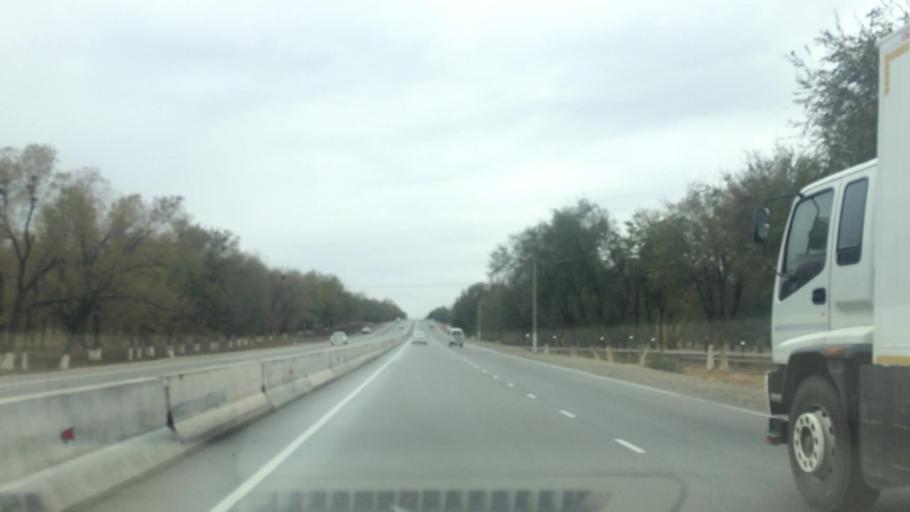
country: UZ
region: Samarqand
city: Bulung'ur
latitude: 39.8952
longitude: 67.4970
